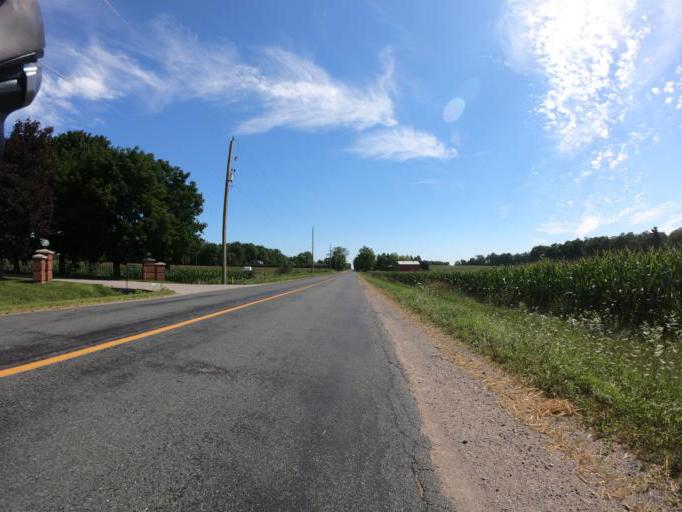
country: CA
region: Ontario
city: Waterloo
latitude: 43.4931
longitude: -80.4394
